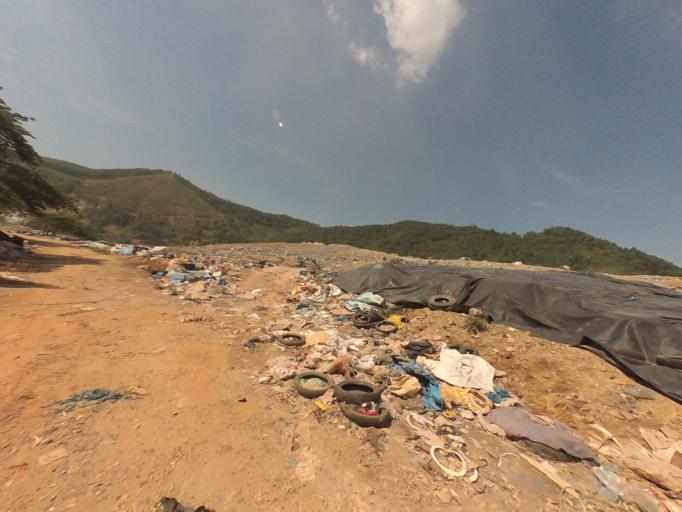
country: VN
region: Da Nang
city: Lien Chieu
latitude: 16.0424
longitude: 108.1431
